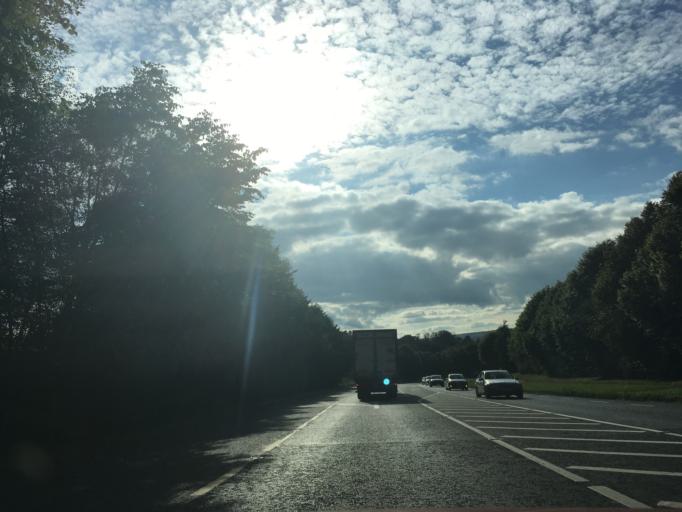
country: IE
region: Leinster
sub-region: Loch Garman
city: New Ross
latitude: 52.3818
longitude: -6.9399
